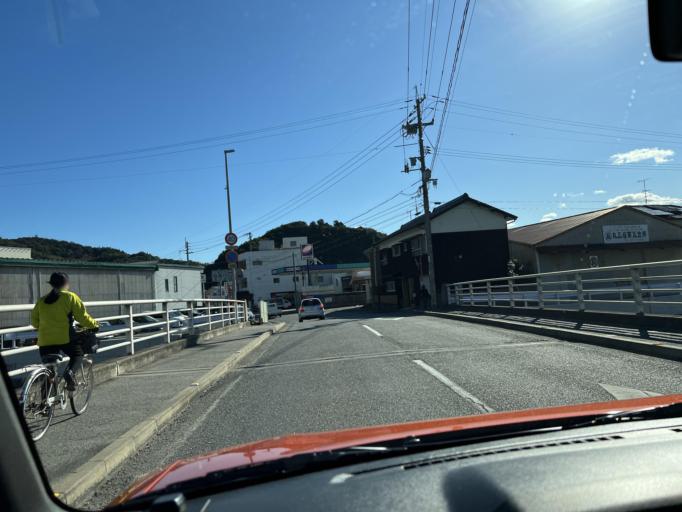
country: JP
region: Kagawa
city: Tonosho
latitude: 34.4883
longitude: 134.1909
